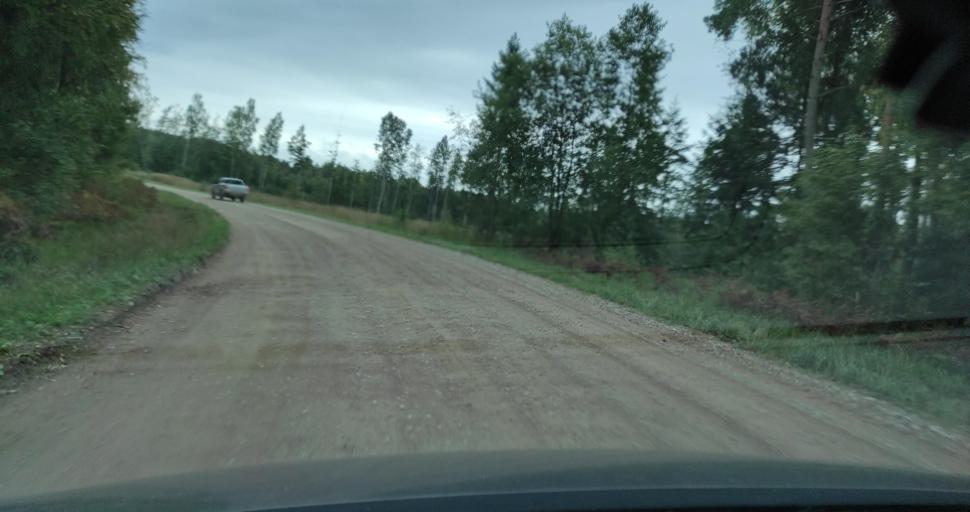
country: LV
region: Talsu Rajons
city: Stende
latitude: 57.0401
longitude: 22.3093
